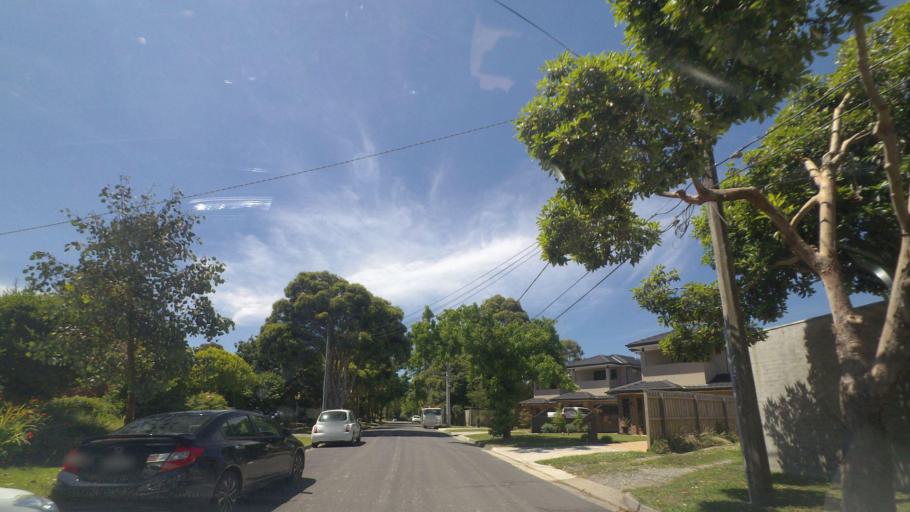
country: AU
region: Victoria
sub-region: Maroondah
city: Ringwood East
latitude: -37.8052
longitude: 145.2270
